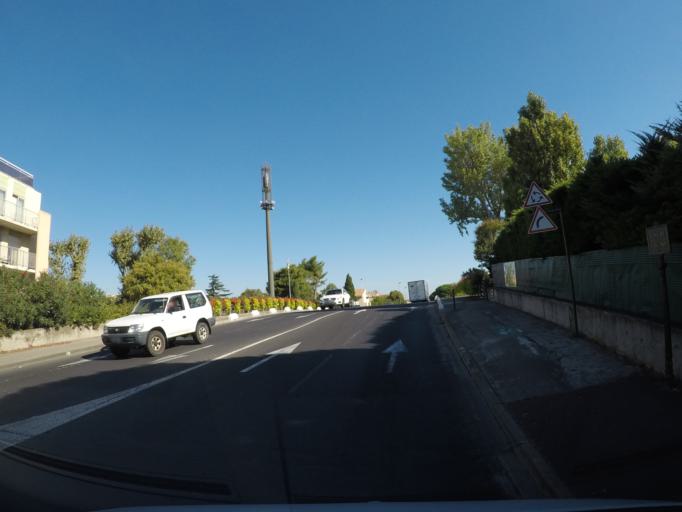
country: FR
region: Languedoc-Roussillon
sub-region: Departement de l'Aude
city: Narbonne
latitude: 43.1796
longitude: 3.0133
